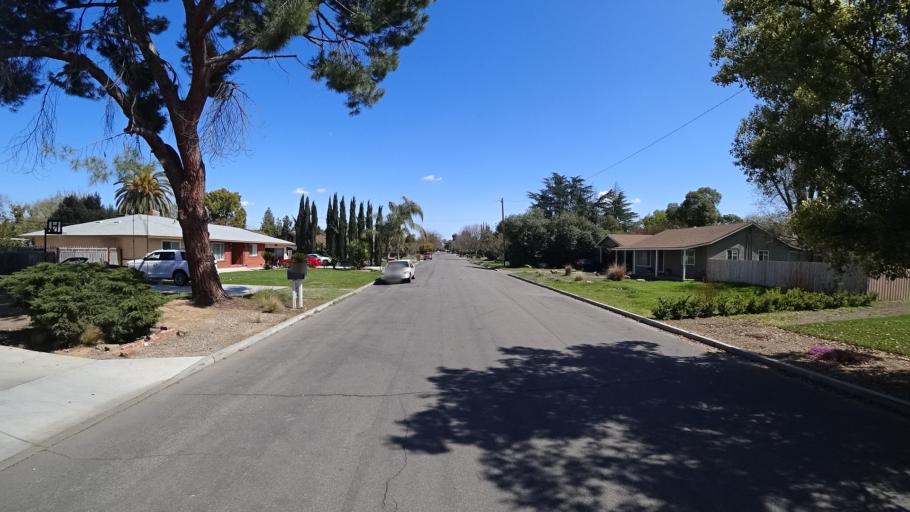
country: US
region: California
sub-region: Fresno County
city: Fresno
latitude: 36.8047
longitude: -119.8256
